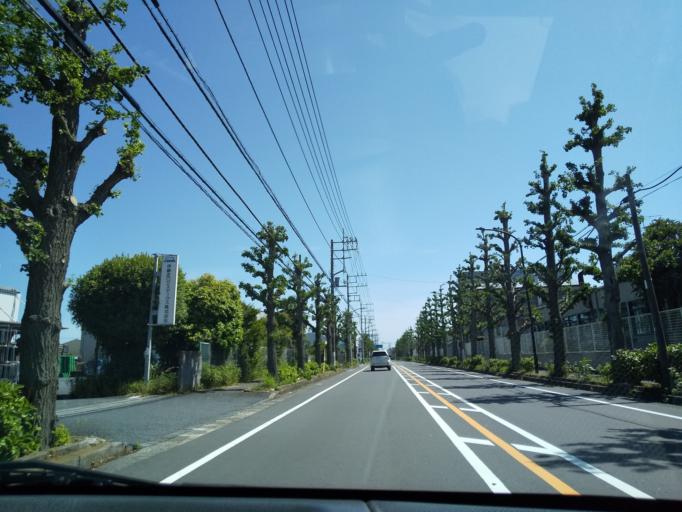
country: JP
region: Tokyo
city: Hachioji
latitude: 35.5739
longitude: 139.3546
